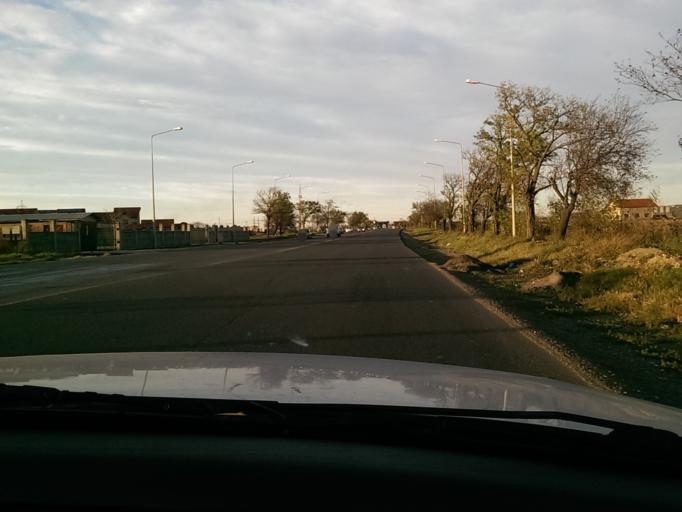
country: RO
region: Bihor
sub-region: Comuna Sanmartin
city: Sanmartin
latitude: 47.0163
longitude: 21.9641
